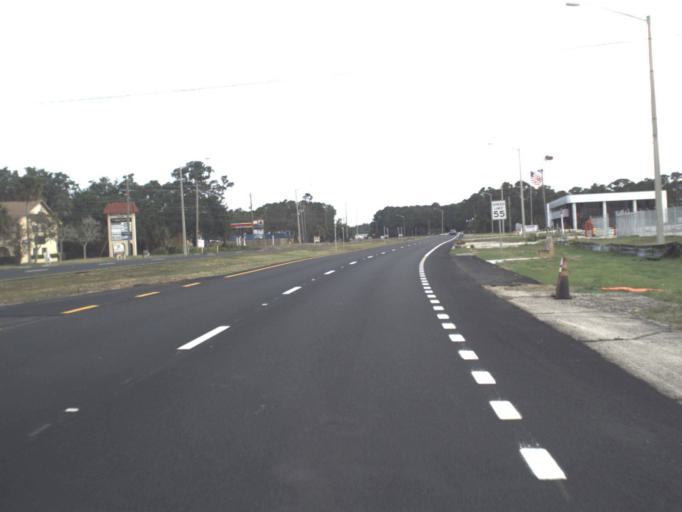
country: US
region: Florida
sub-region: Brevard County
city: Titusville
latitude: 28.5514
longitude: -80.7961
